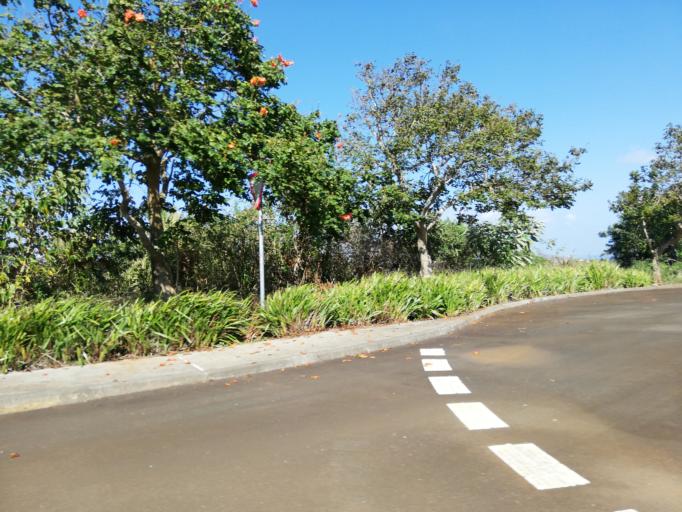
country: MU
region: Moka
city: Moka
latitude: -20.2217
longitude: 57.4914
